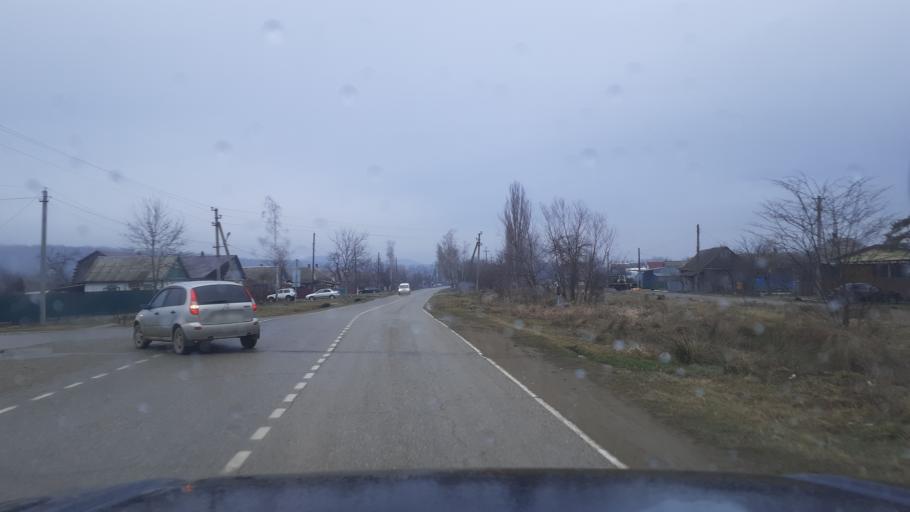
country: RU
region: Krasnodarskiy
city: Neftegorsk
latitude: 44.2497
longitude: 39.7667
